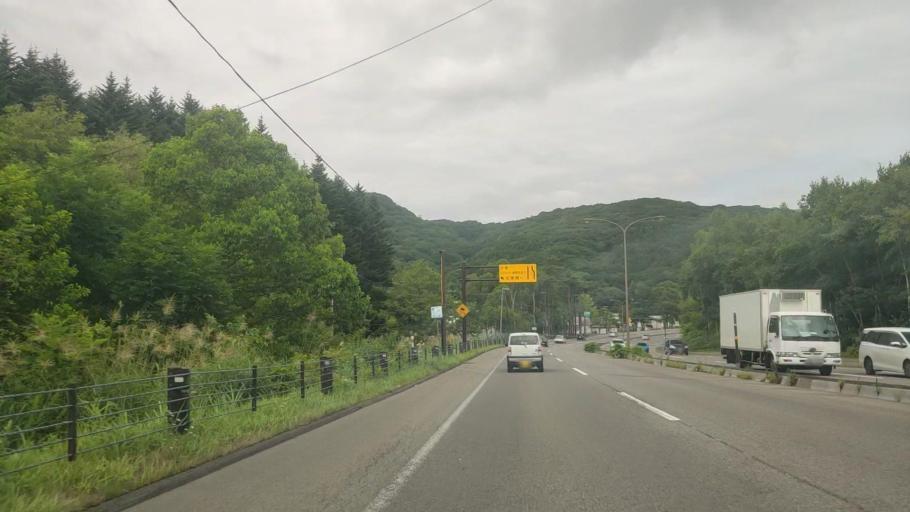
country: JP
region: Hokkaido
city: Nanae
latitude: 41.9591
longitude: 140.6486
